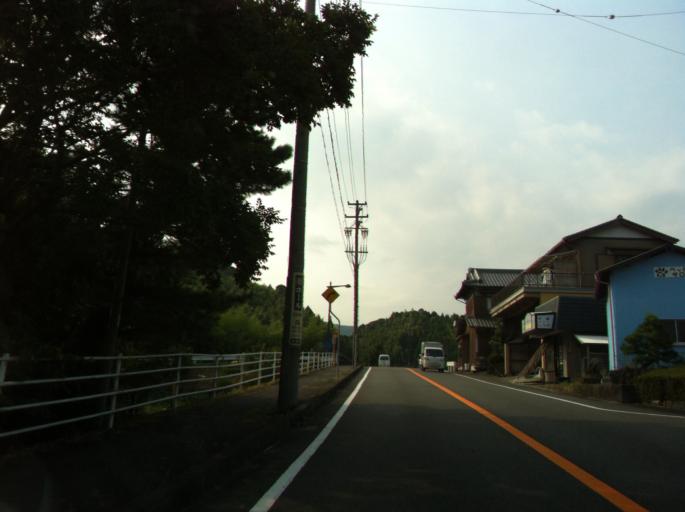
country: JP
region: Shizuoka
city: Fujieda
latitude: 34.9418
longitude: 138.2587
